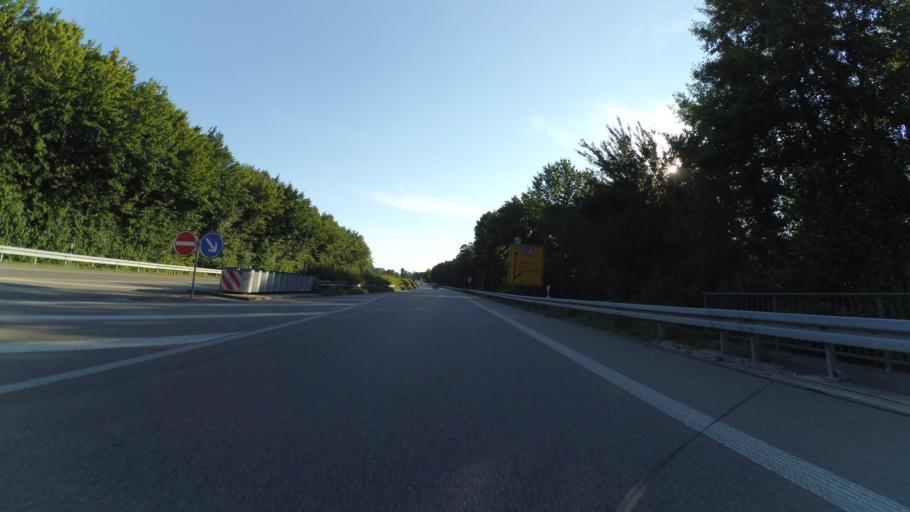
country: DE
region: Baden-Wuerttemberg
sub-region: Freiburg Region
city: Waldkirch
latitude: 48.0852
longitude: 7.9503
